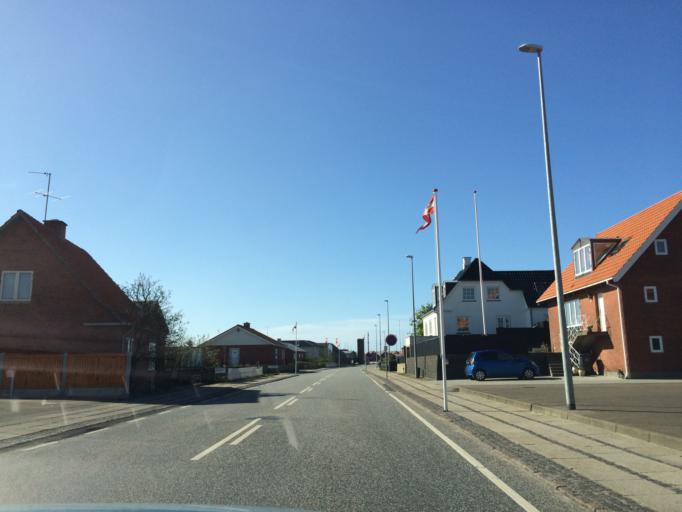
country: DK
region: Central Jutland
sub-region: Ringkobing-Skjern Kommune
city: Hvide Sande
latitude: 56.0075
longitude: 8.1298
